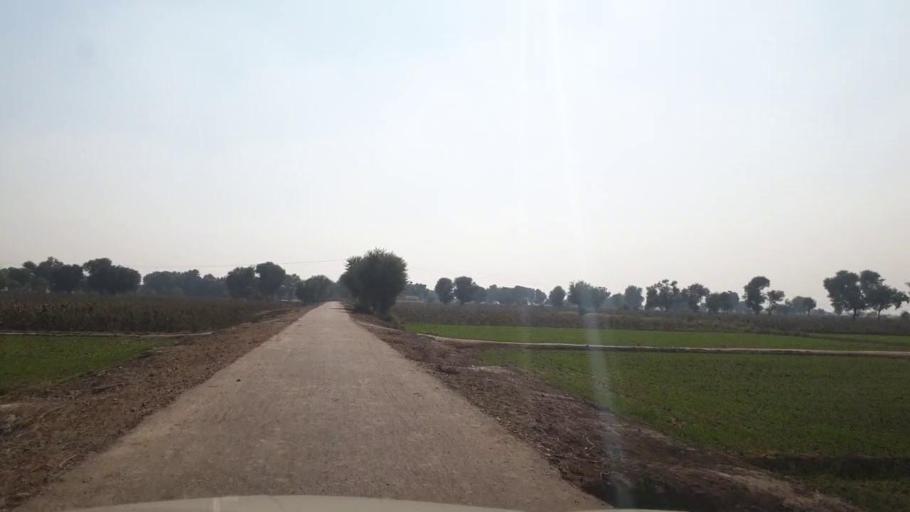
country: PK
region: Sindh
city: Bhan
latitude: 26.5336
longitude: 67.7632
